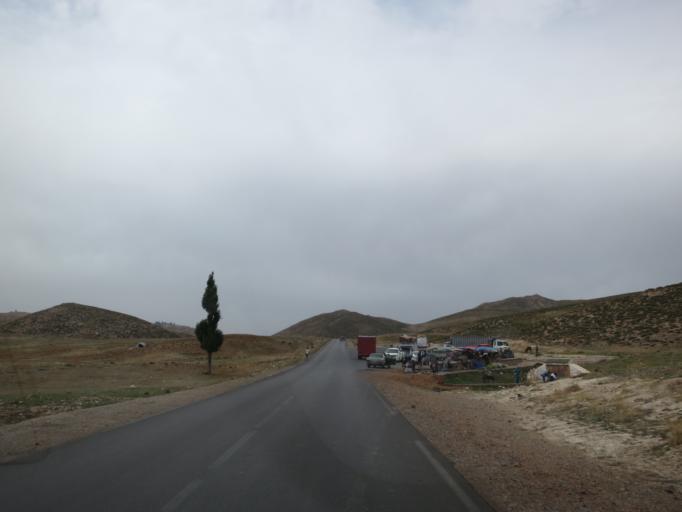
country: MA
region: Meknes-Tafilalet
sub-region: Khenifra
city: Itzer
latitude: 33.0447
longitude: -5.0521
